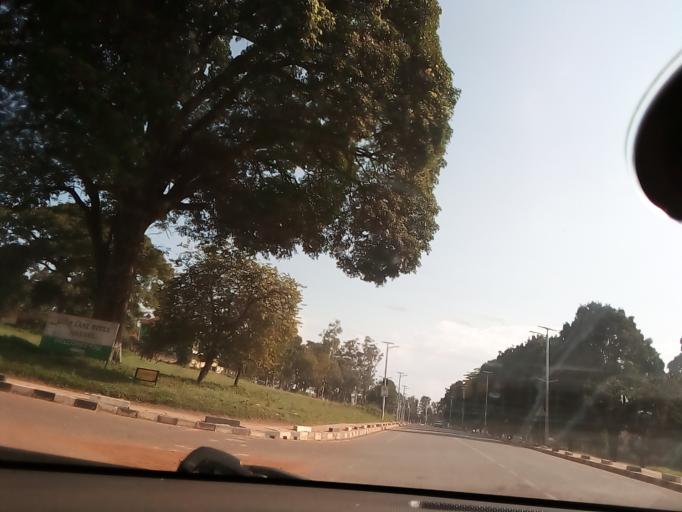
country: UG
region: Central Region
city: Masaka
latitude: -0.3328
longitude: 31.7379
